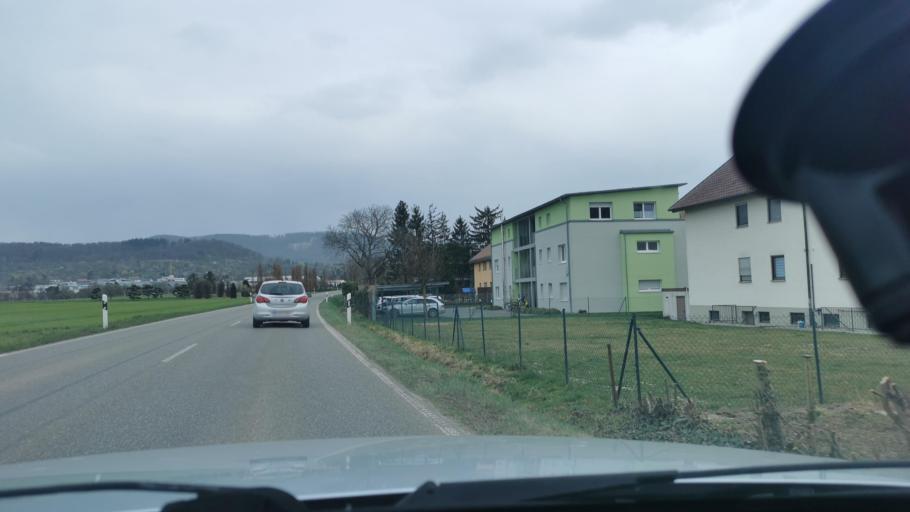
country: DE
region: Baden-Wuerttemberg
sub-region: Regierungsbezirk Stuttgart
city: Weilheim an der Teck
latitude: 48.6241
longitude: 9.5331
